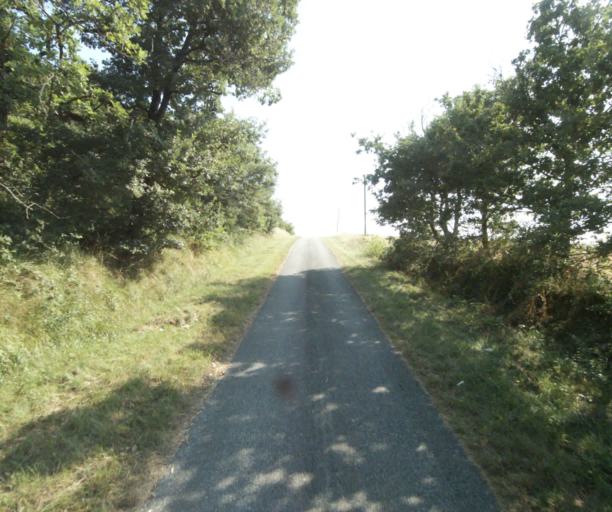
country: FR
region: Midi-Pyrenees
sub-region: Departement de la Haute-Garonne
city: Saint-Felix-Lauragais
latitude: 43.4235
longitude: 1.8315
